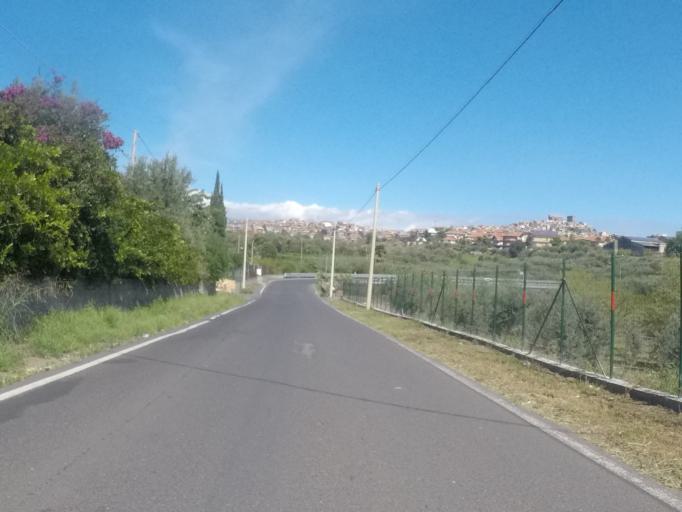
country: IT
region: Sicily
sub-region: Catania
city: Motta Sant'Anastasia
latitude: 37.5030
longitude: 14.9592
